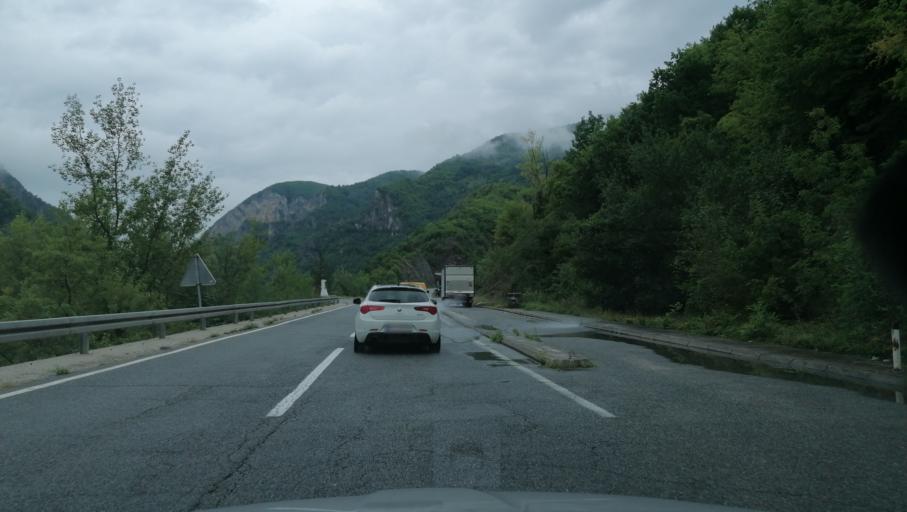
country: BA
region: Republika Srpska
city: Visegrad
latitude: 43.7521
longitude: 19.2355
